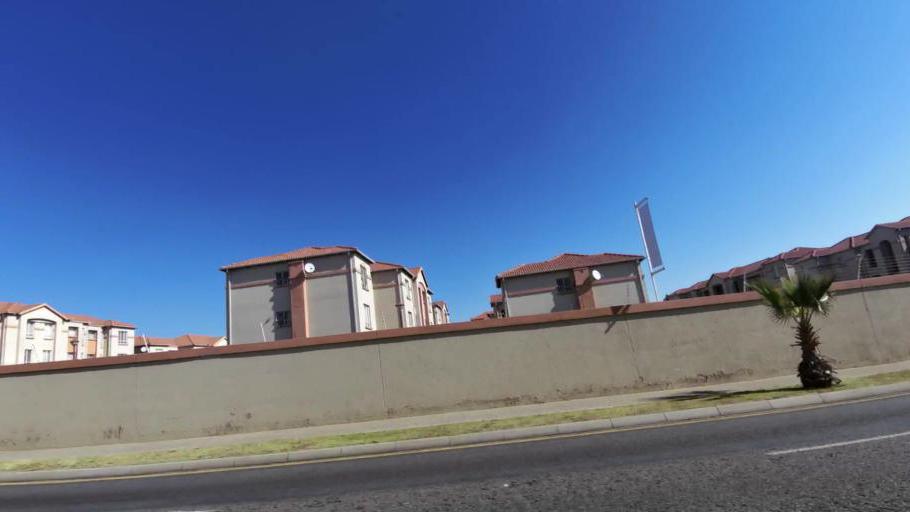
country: ZA
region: Gauteng
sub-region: City of Johannesburg Metropolitan Municipality
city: Johannesburg
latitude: -26.2538
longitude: 27.9853
